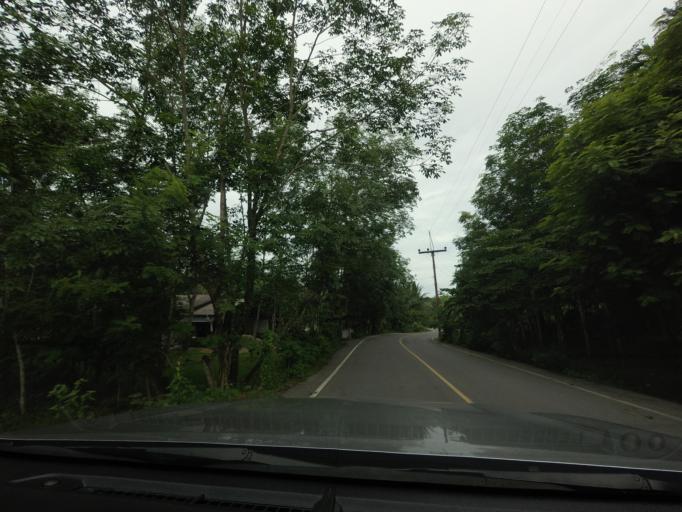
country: TH
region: Nakhon Si Thammarat
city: Phra Phrom
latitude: 8.2813
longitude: 99.9369
